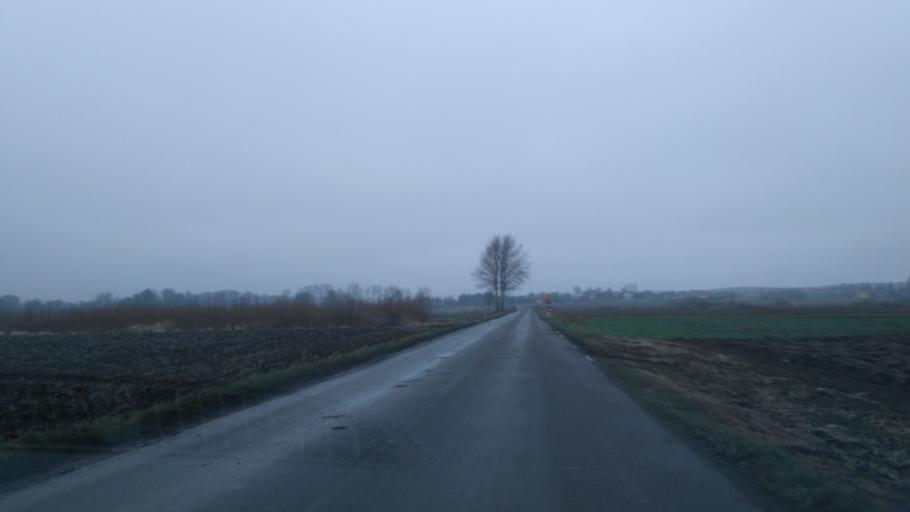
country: PL
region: Subcarpathian Voivodeship
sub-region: Powiat przeworski
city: Zarzecze
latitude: 49.9783
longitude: 22.5527
